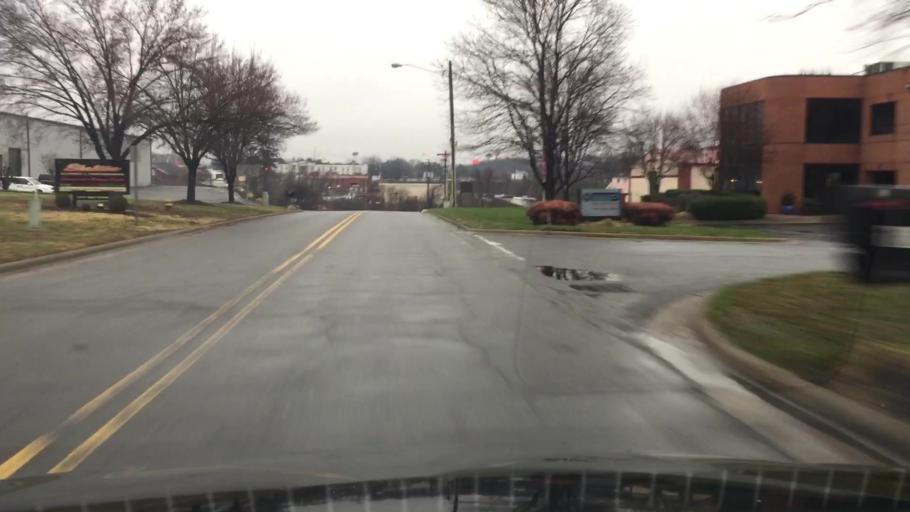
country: US
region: North Carolina
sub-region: Iredell County
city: Mooresville
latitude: 35.5904
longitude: -80.8631
